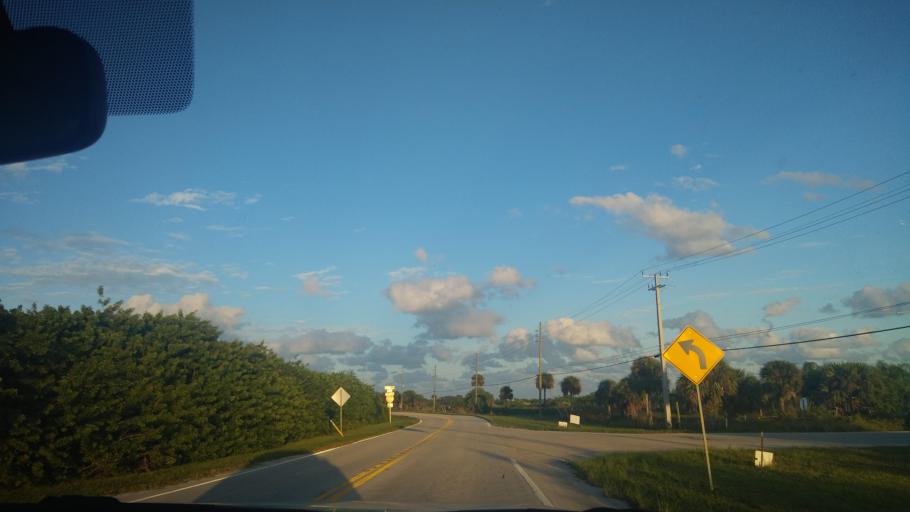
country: US
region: Florida
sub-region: Indian River County
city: Fellsmere
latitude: 27.7400
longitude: -80.6415
